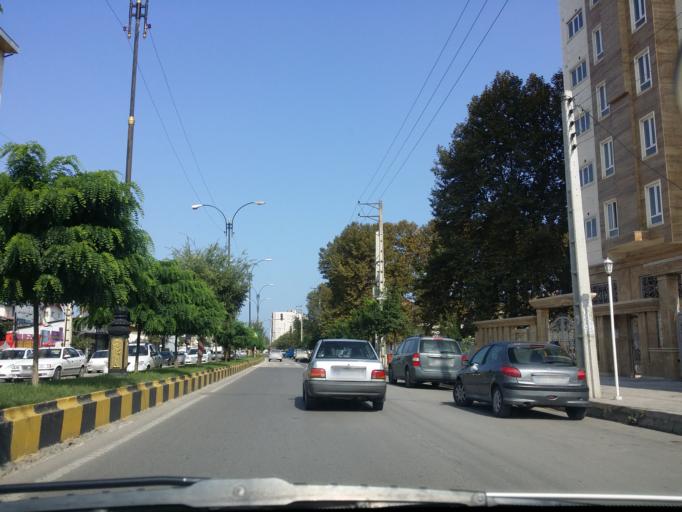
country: IR
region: Mazandaran
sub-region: Nowshahr
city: Nowshahr
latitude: 36.6401
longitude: 51.4906
